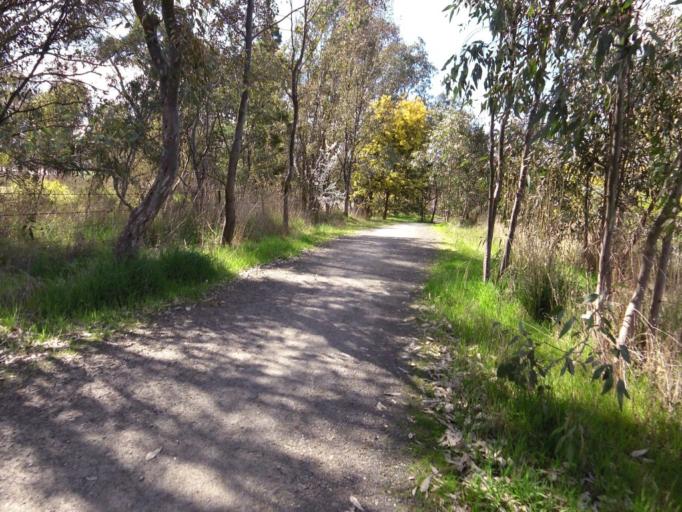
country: AU
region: Victoria
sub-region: Mansfield
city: Mansfield
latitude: -37.0497
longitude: 146.0722
